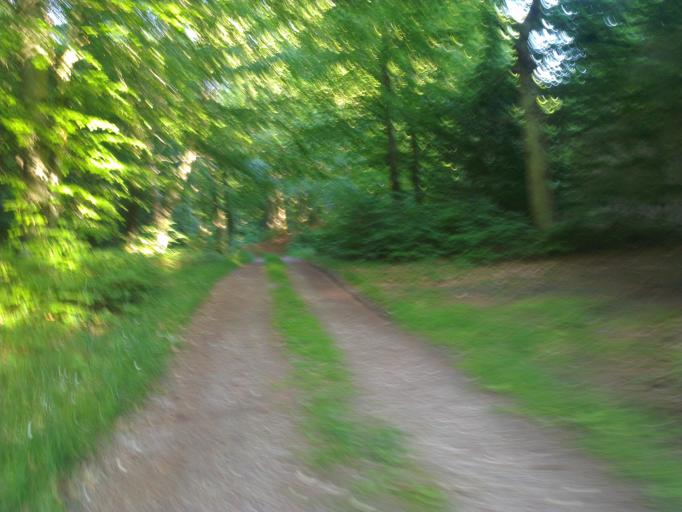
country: DK
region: Capital Region
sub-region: Frederikssund Kommune
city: Jaegerspris
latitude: 55.8937
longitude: 12.0016
